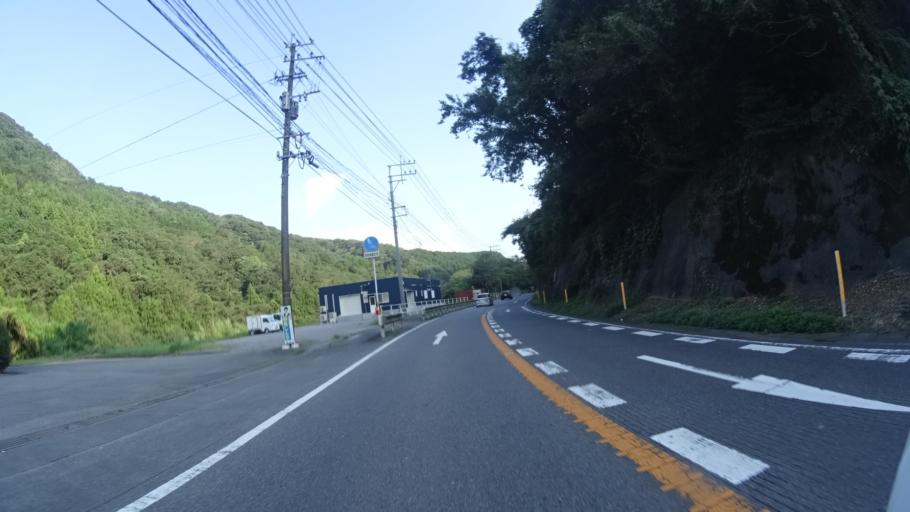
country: JP
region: Oita
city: Bungo-Takada-shi
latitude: 33.4890
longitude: 131.3340
